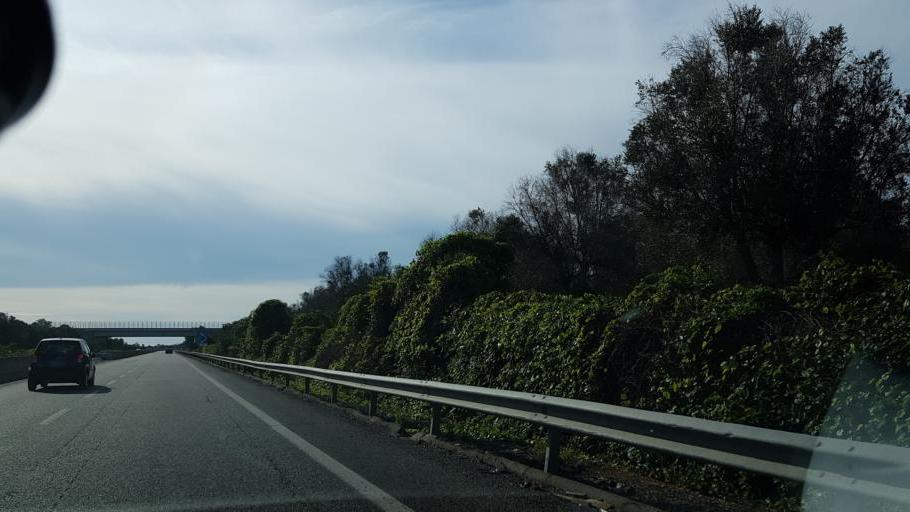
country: IT
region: Apulia
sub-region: Provincia di Brindisi
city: San Pietro Vernotico
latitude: 40.5375
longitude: 18.0052
